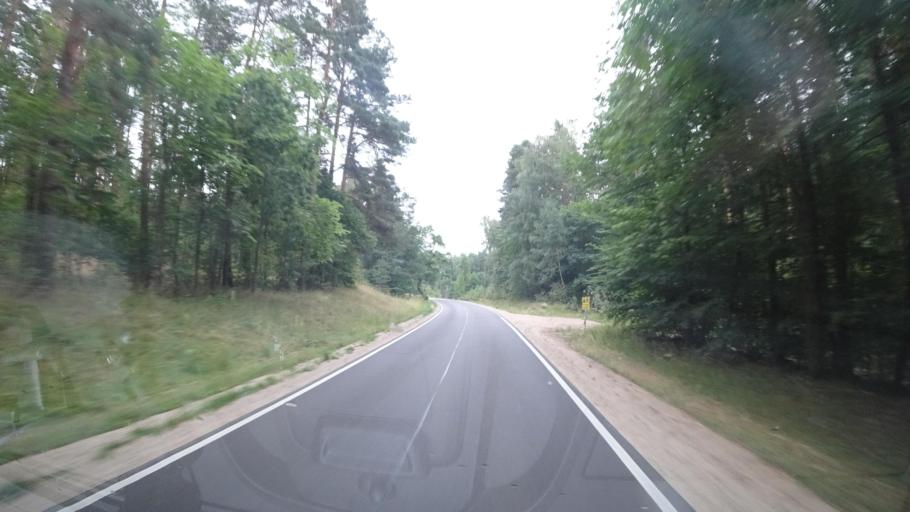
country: PL
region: Warmian-Masurian Voivodeship
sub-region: Powiat gizycki
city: Ryn
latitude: 53.8877
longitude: 21.5754
